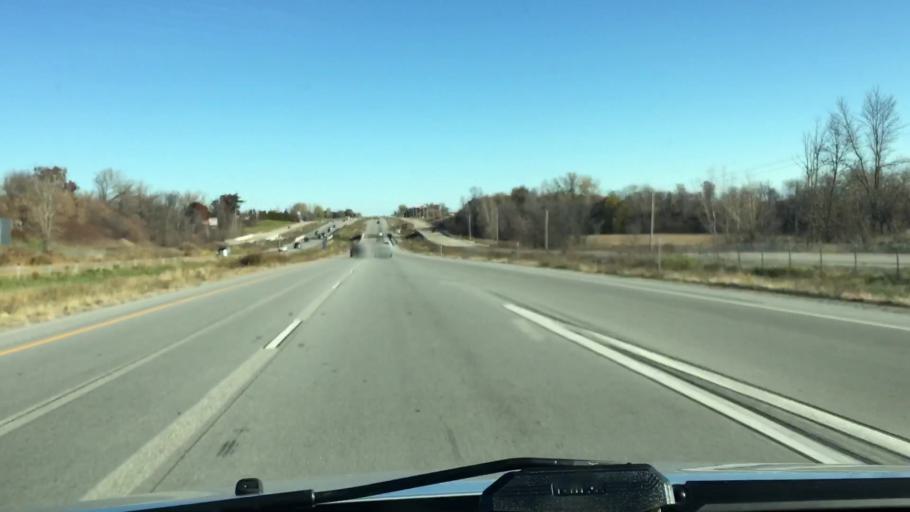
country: US
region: Wisconsin
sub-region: Brown County
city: Wrightstown
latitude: 44.3523
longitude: -88.1904
